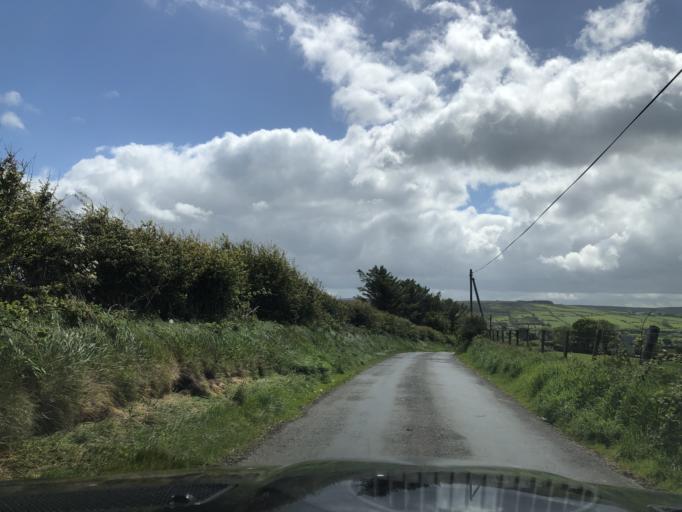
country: GB
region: Northern Ireland
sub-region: Moyle District
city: Ballycastle
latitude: 55.2033
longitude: -6.1722
